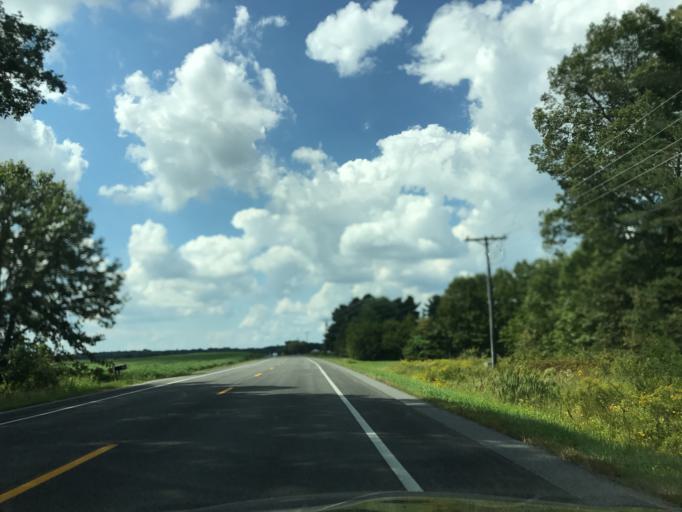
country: US
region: Maryland
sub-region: Queen Anne's County
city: Kingstown
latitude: 39.1468
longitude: -75.8813
